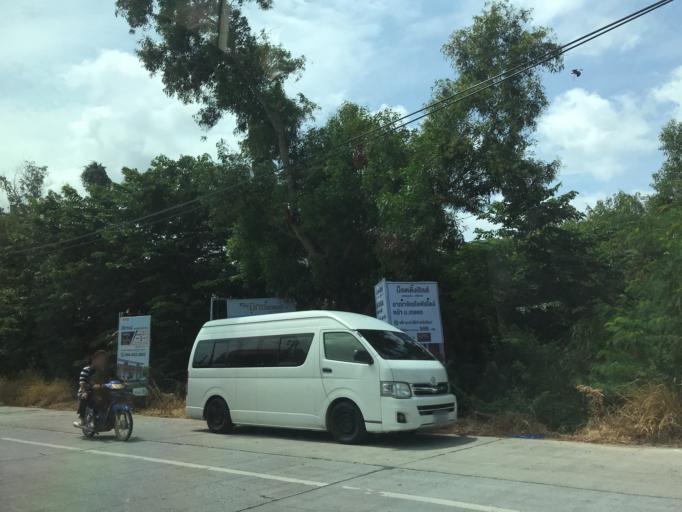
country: TH
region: Chon Buri
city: Si Racha
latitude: 13.1492
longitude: 100.9669
